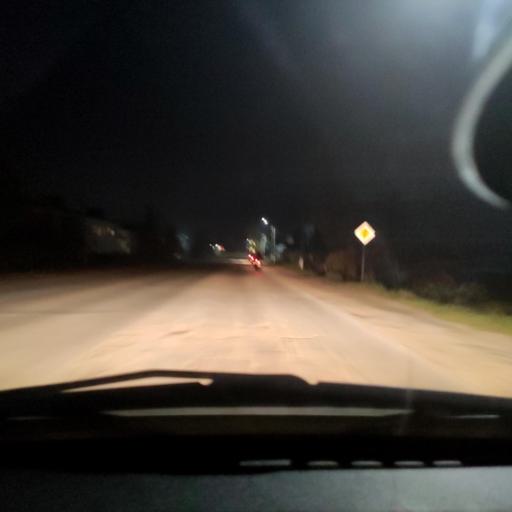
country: RU
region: Bashkortostan
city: Iglino
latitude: 54.8333
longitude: 56.4109
